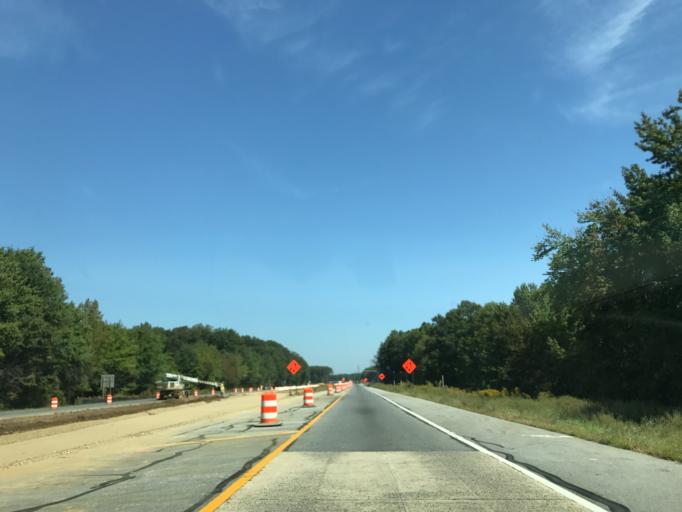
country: US
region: Delaware
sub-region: New Castle County
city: Middletown
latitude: 39.4056
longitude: -75.7764
